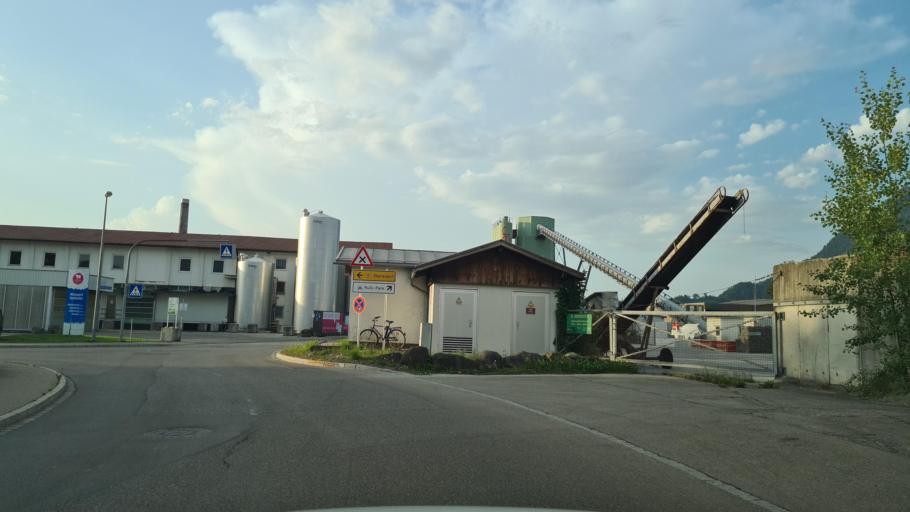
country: DE
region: Bavaria
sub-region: Swabia
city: Sonthofen
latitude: 47.5183
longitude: 10.2714
